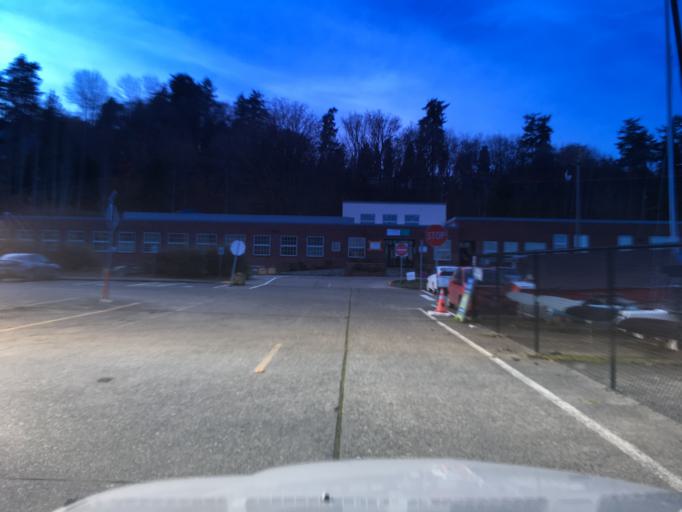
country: US
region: Washington
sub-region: King County
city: Inglewood-Finn Hill
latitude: 47.6875
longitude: -122.2641
